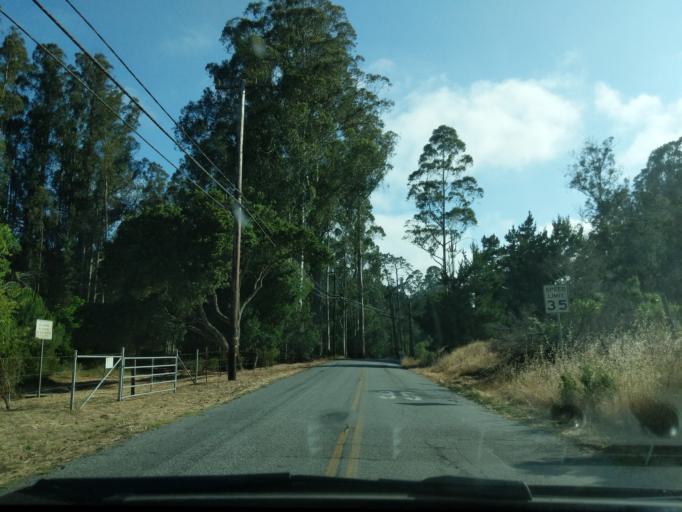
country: US
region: California
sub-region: Monterey County
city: Prunedale
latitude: 36.7990
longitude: -121.6441
